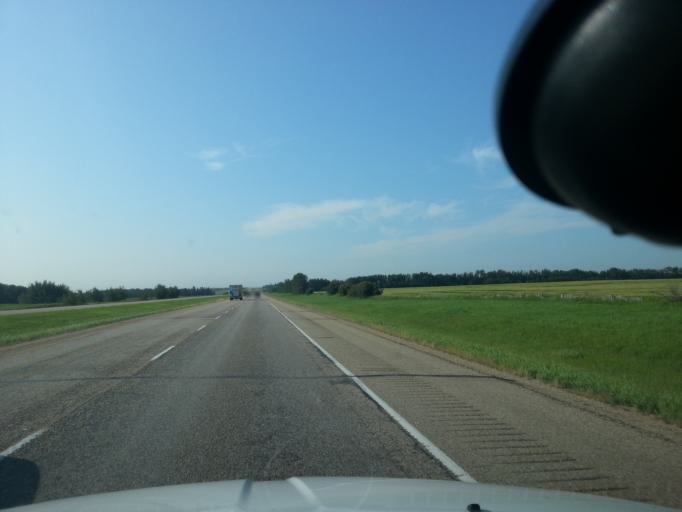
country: CA
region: Alberta
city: Ponoka
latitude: 52.8632
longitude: -113.6442
